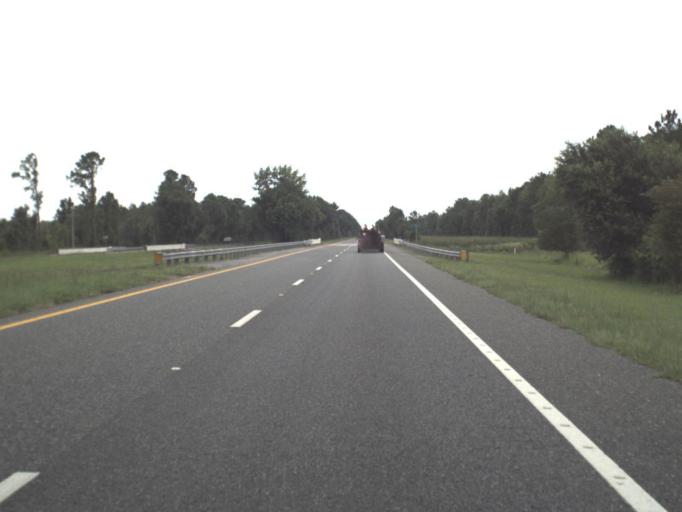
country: US
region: Florida
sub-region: Levy County
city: Bronson
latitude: 29.2908
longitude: -82.7460
